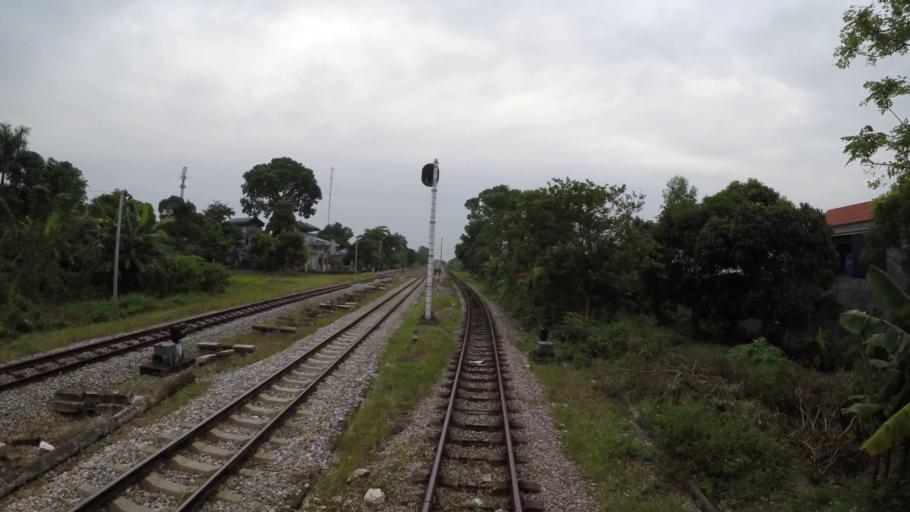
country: VN
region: Hai Duong
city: Ke Sat
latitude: 20.9666
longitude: 106.1478
